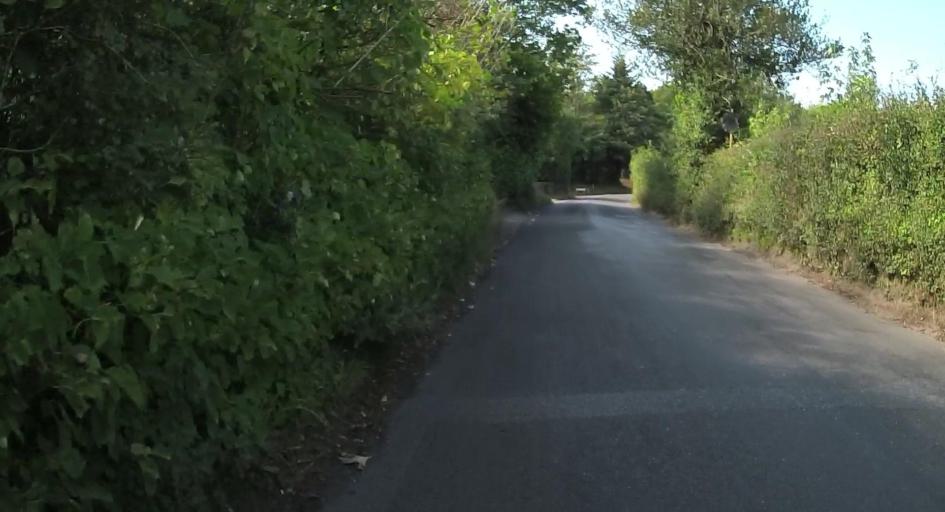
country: GB
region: England
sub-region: Surrey
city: Farnham
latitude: 51.1780
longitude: -0.7945
